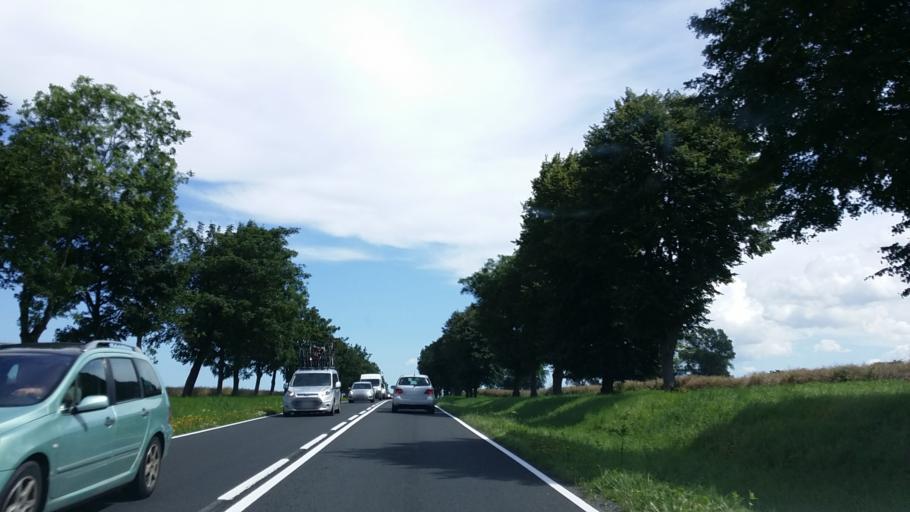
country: PL
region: West Pomeranian Voivodeship
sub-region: Powiat kolobrzeski
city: Ustronie Morskie
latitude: 54.2025
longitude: 15.8953
